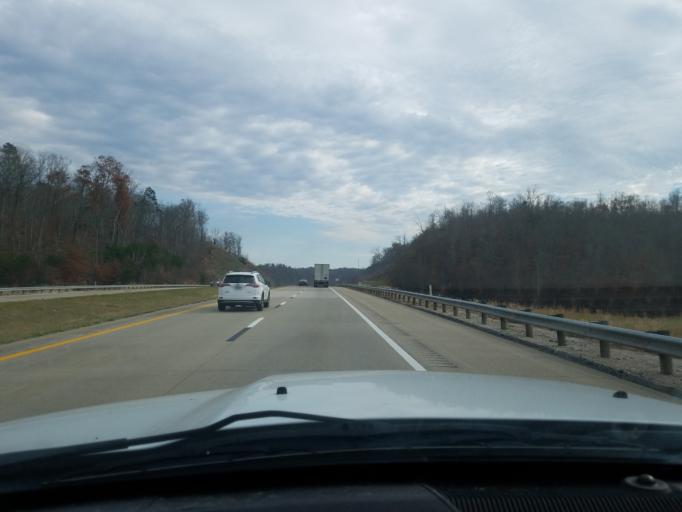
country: US
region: West Virginia
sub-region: Putnam County
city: Eleanor
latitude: 38.5290
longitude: -81.9455
